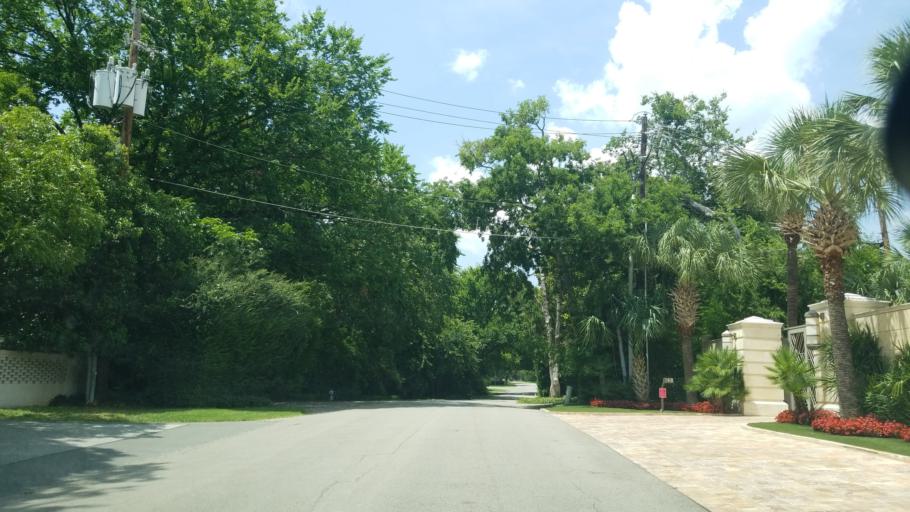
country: US
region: Texas
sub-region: Dallas County
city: University Park
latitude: 32.8694
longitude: -96.8086
